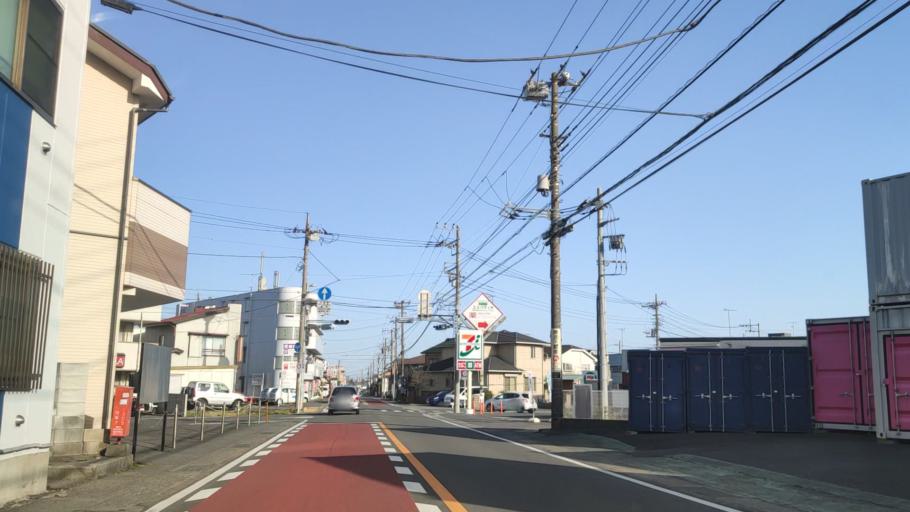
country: JP
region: Kanagawa
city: Zama
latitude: 35.5020
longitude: 139.3562
